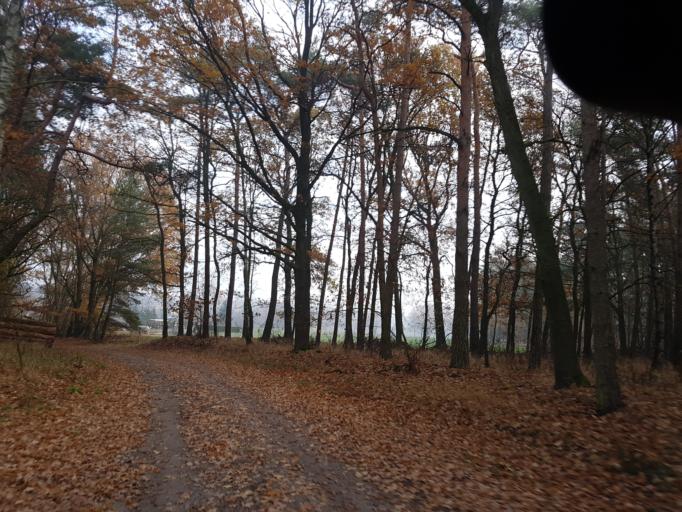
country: DE
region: Saxony-Anhalt
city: Kropstadt
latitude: 51.9324
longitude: 12.7546
